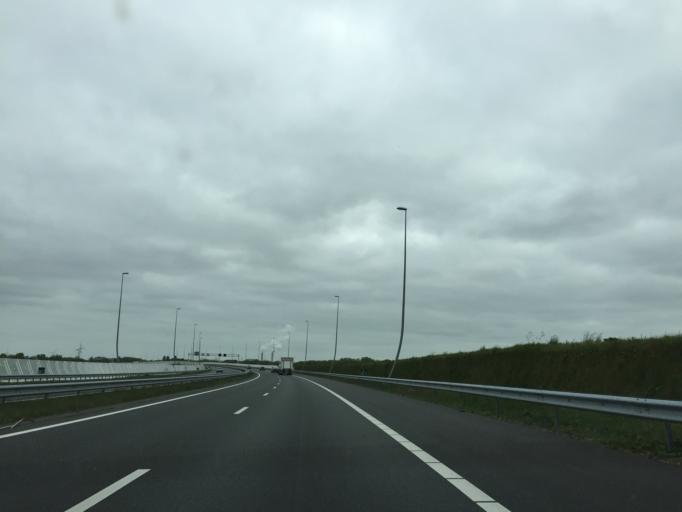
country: NL
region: North Holland
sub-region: Gemeente Zaanstad
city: Zaandam
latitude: 52.3719
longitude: 4.7635
